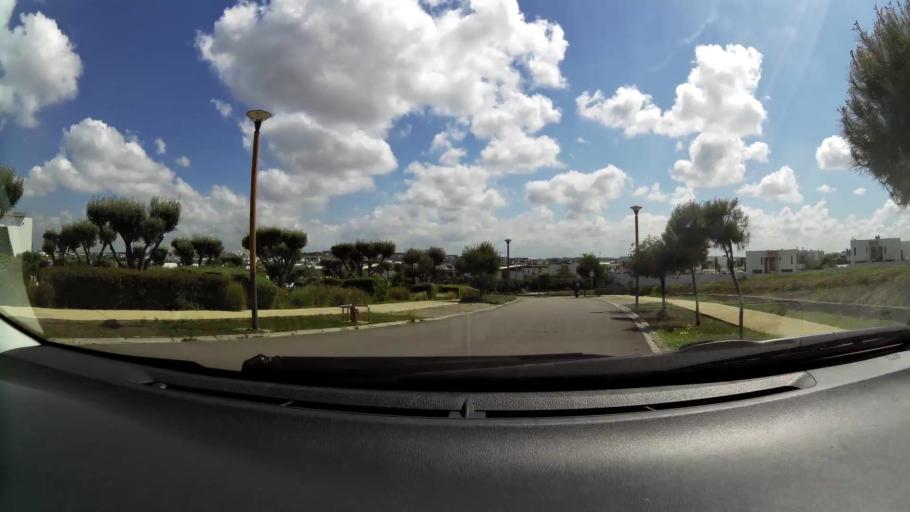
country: MA
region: Grand Casablanca
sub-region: Nouaceur
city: Bouskoura
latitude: 33.4910
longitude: -7.6000
